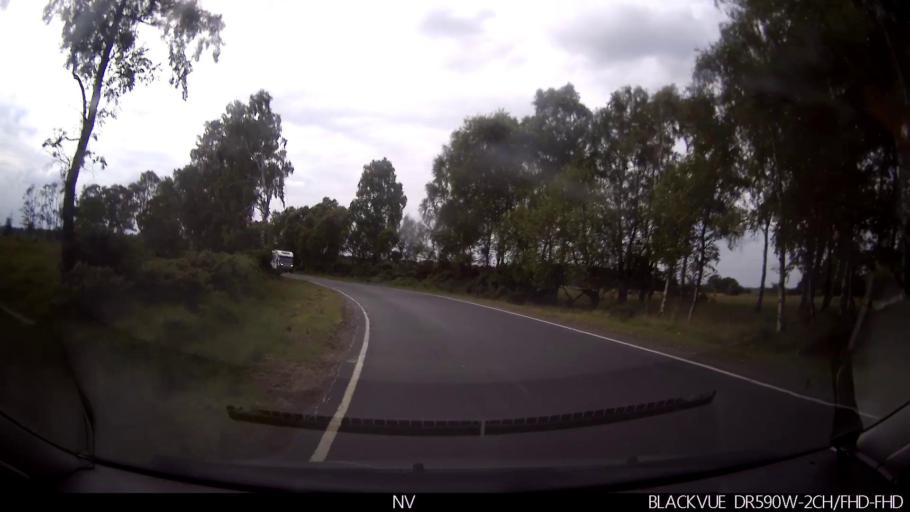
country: GB
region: England
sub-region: North Yorkshire
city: Strensall
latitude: 54.0467
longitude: -0.9962
